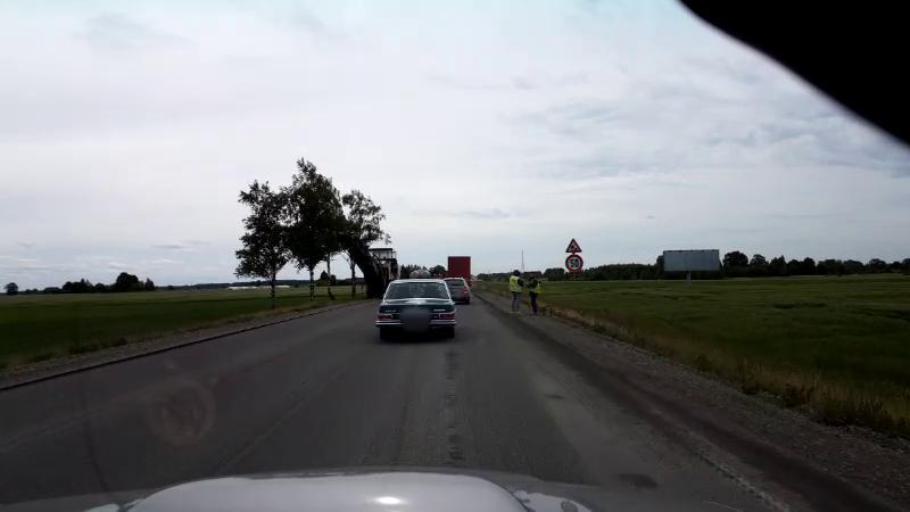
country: LV
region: Bauskas Rajons
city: Bauska
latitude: 56.2867
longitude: 24.3575
